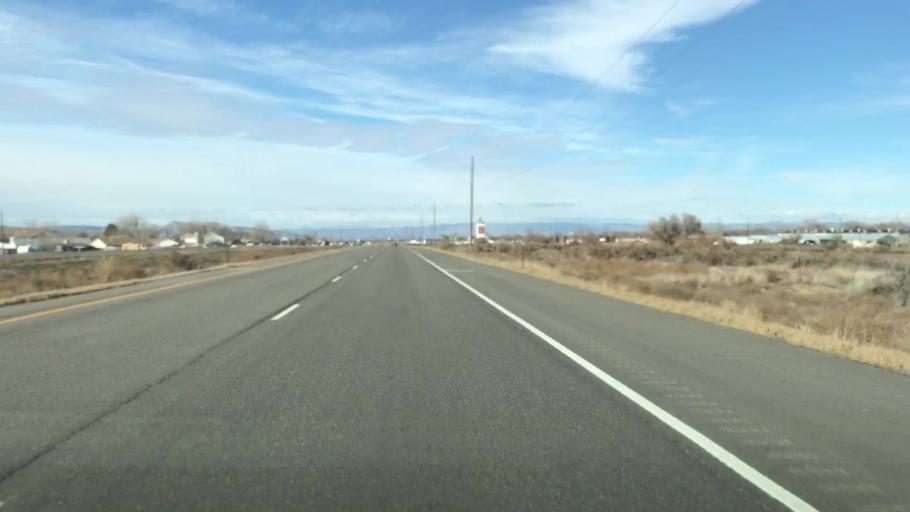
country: US
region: Colorado
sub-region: Mesa County
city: Fruita
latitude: 39.1480
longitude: -108.7211
